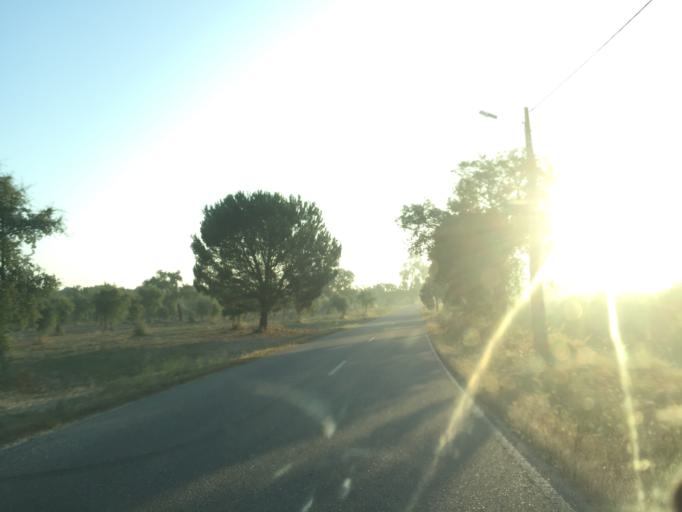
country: PT
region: Santarem
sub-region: Coruche
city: Coruche
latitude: 39.0583
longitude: -8.4155
